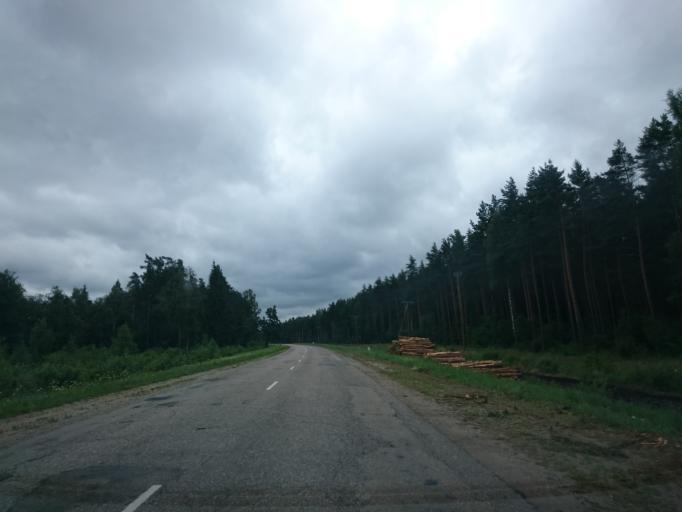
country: LV
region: Pavilostas
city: Pavilosta
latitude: 56.7823
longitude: 21.2489
